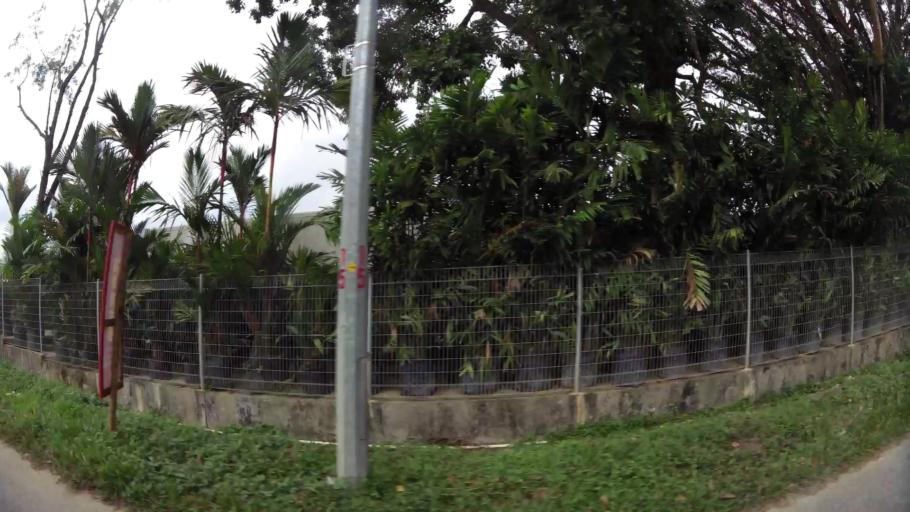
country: MY
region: Johor
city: Kampung Pasir Gudang Baru
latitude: 1.4190
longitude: 103.8282
